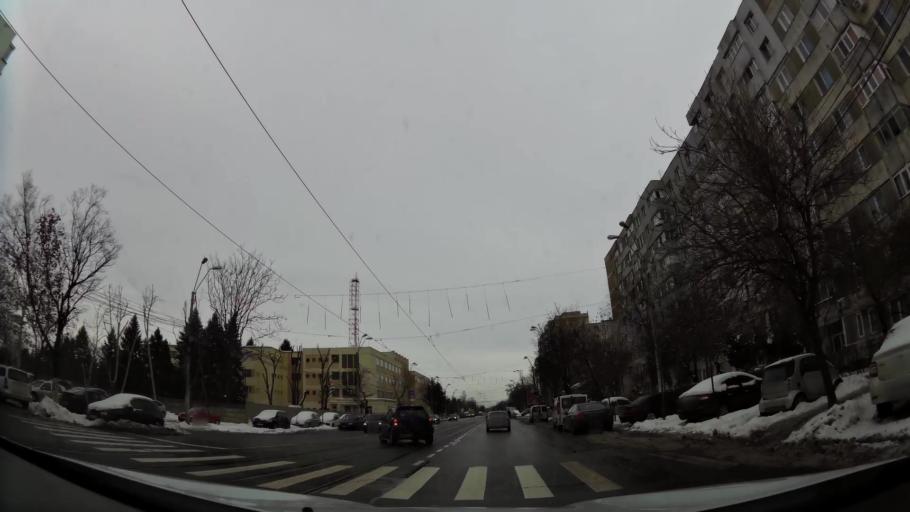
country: RO
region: Ilfov
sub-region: Comuna Popesti-Leordeni
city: Popesti-Leordeni
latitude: 44.3876
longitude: 26.1357
